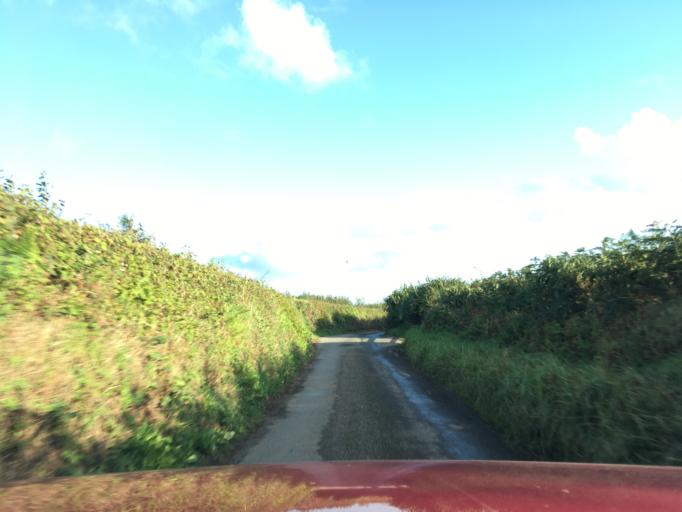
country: GB
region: England
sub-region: Devon
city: Dartmouth
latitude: 50.3450
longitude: -3.6107
